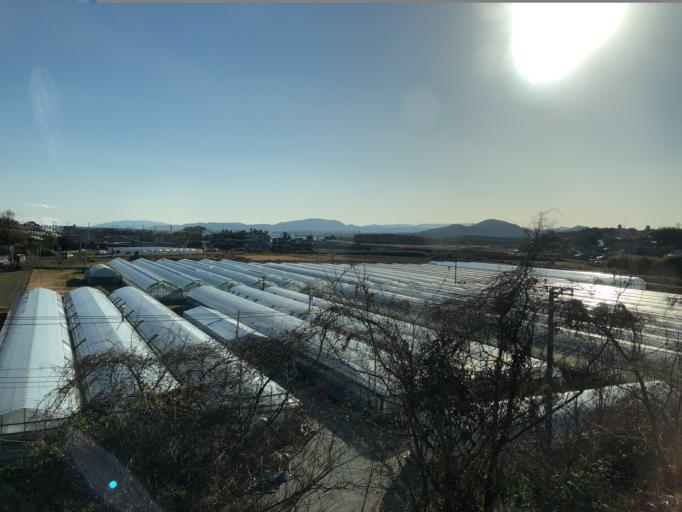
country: JP
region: Kochi
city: Nakamura
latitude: 33.0395
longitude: 133.0298
